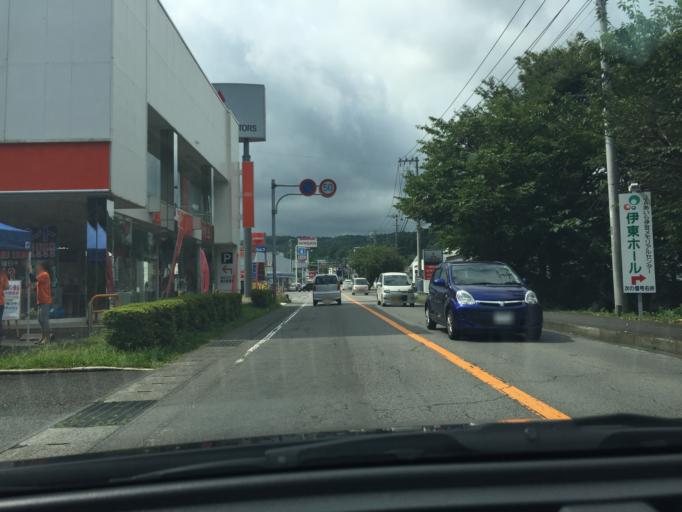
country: JP
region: Shizuoka
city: Ito
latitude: 34.9429
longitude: 139.1175
